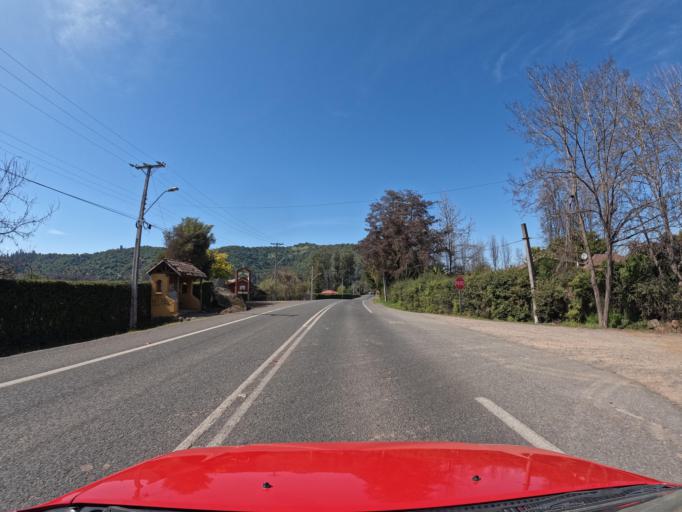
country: CL
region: Maule
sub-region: Provincia de Curico
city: Teno
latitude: -34.9783
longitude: -70.9900
